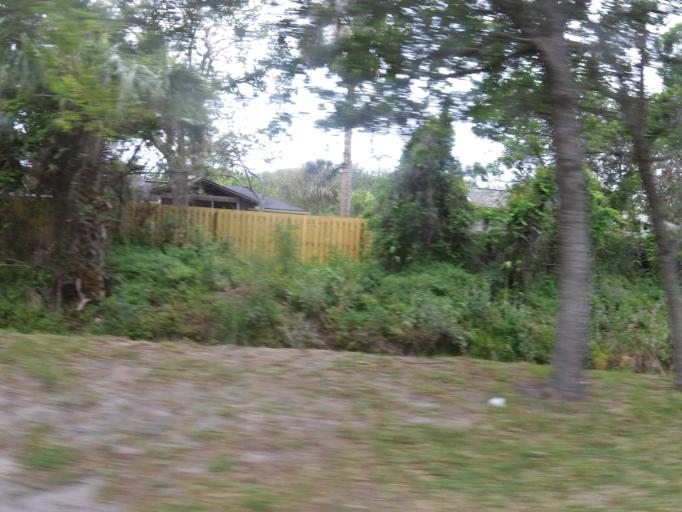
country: US
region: Florida
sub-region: Duval County
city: Atlantic Beach
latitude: 30.3427
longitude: -81.3992
